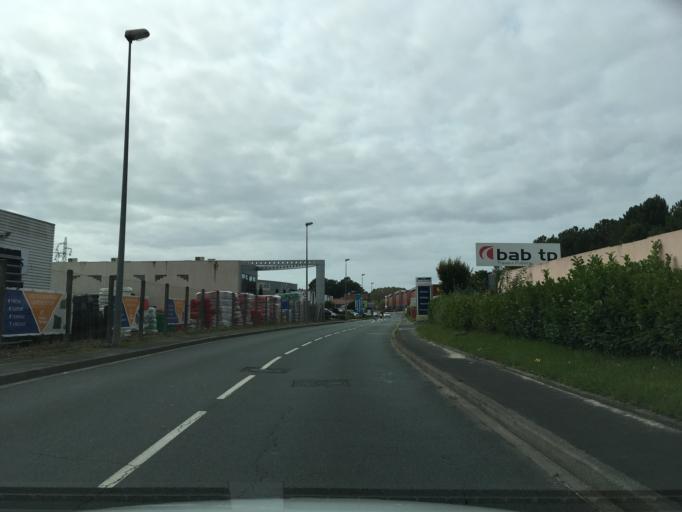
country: FR
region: Aquitaine
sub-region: Departement des Pyrenees-Atlantiques
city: Anglet
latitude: 43.4633
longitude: -1.5095
